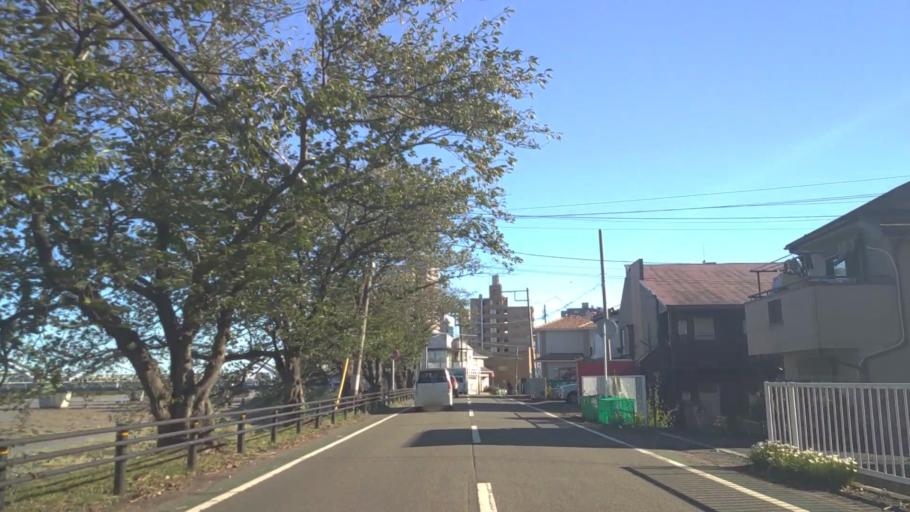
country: JP
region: Kanagawa
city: Atsugi
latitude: 35.4475
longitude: 139.3686
